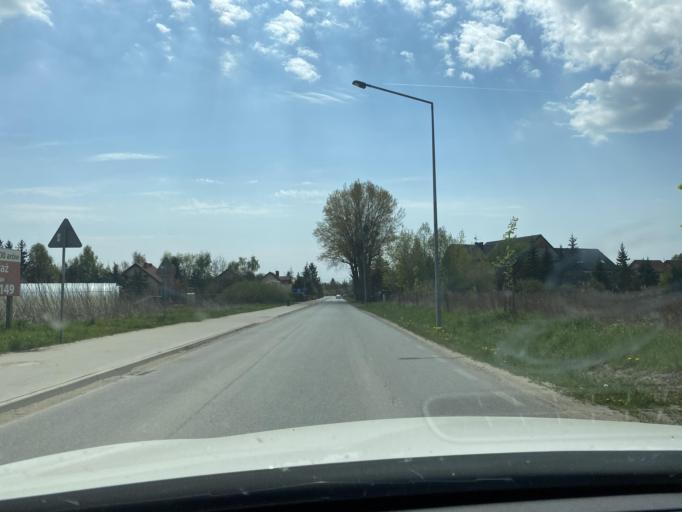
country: PL
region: Lower Silesian Voivodeship
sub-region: Powiat wroclawski
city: Mirkow
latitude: 51.1644
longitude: 17.1649
